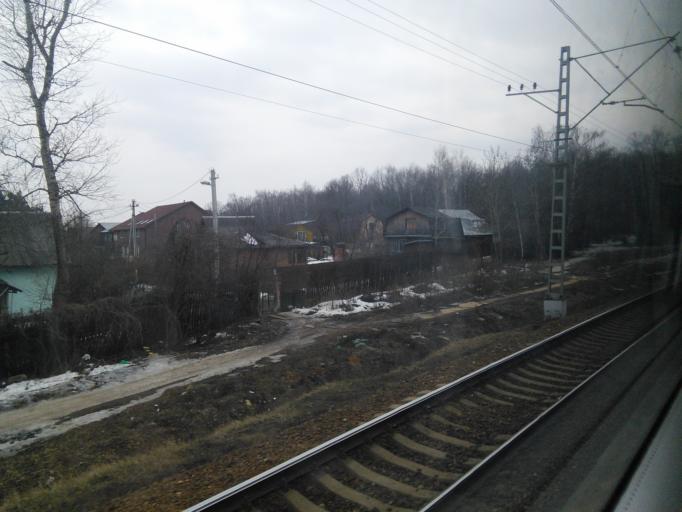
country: RU
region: Moskovskaya
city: Vostryakovo
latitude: 55.4166
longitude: 37.8262
